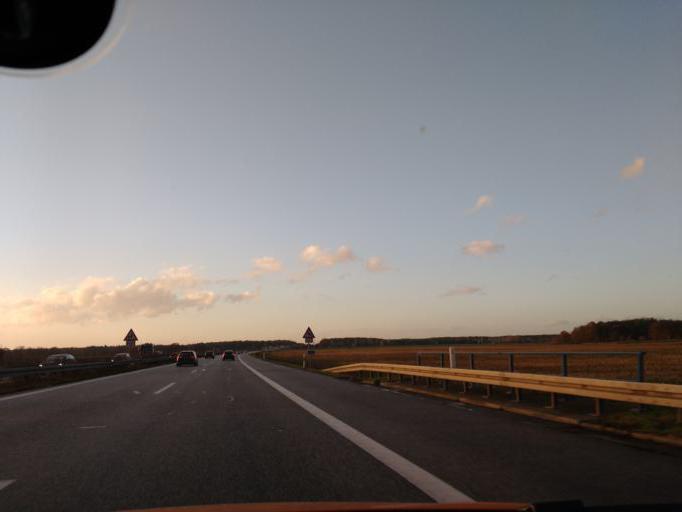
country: DE
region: Mecklenburg-Vorpommern
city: Sulstorf
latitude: 53.4718
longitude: 11.3136
